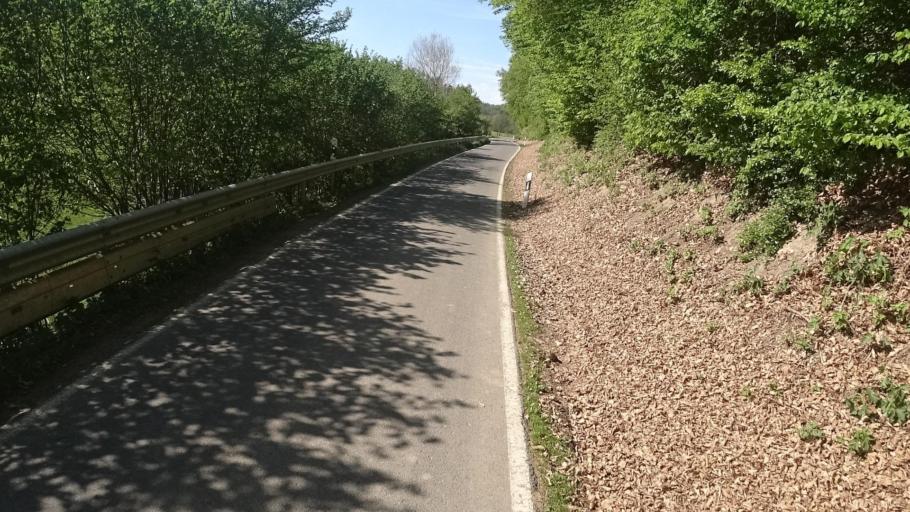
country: DE
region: Rheinland-Pfalz
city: Sierscheid
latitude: 50.4658
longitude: 6.9245
